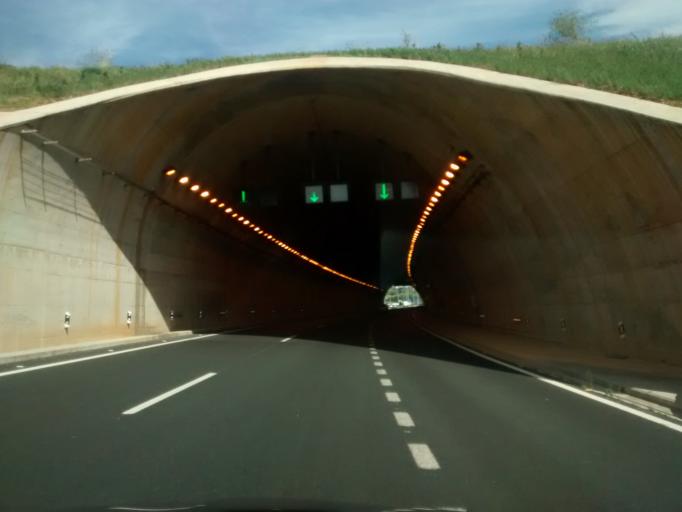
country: ES
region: Cantabria
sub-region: Provincia de Cantabria
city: Camargo
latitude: 43.4117
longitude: -3.8726
